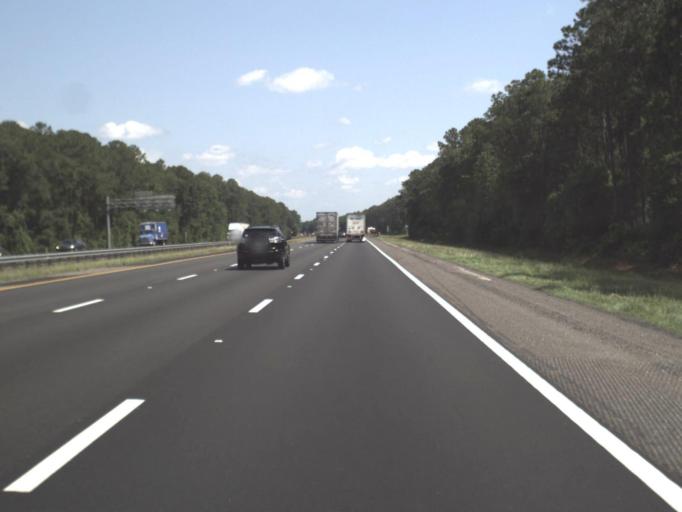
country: US
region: Florida
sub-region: Nassau County
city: Yulee
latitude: 30.5354
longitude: -81.6369
